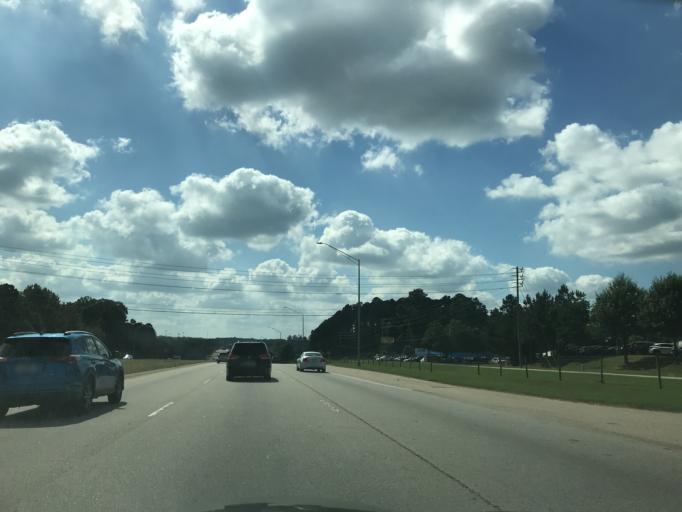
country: US
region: North Carolina
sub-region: Wake County
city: Wake Forest
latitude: 35.8835
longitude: -78.5699
